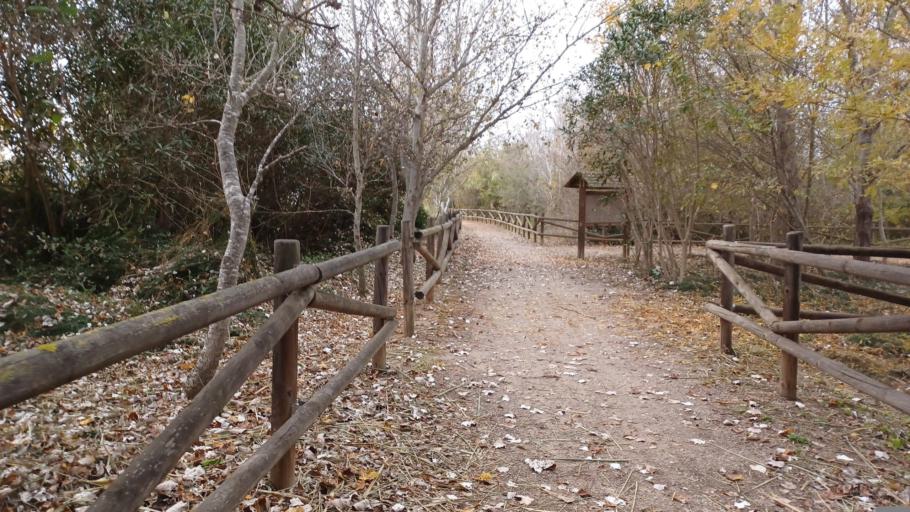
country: ES
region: Catalonia
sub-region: Provincia de Tarragona
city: Amposta
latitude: 40.7053
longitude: 0.6207
